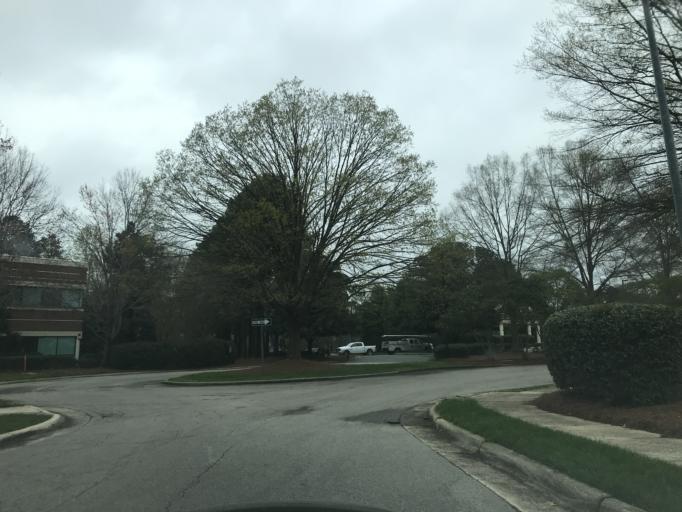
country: US
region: North Carolina
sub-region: Wake County
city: West Raleigh
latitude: 35.8845
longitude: -78.6483
